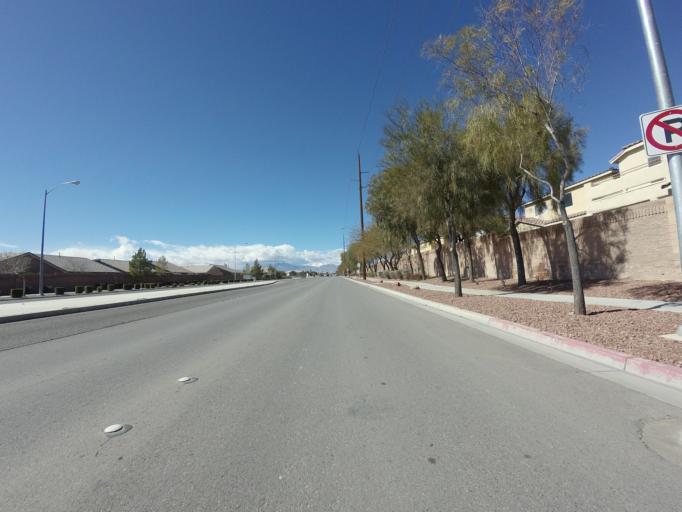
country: US
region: Nevada
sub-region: Clark County
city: Nellis Air Force Base
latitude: 36.2692
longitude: -115.0949
